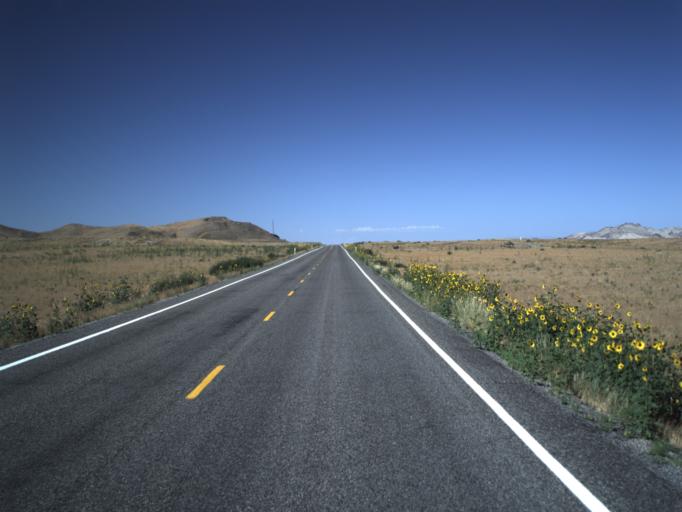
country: US
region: Utah
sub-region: Juab County
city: Nephi
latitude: 39.6696
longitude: -112.2680
